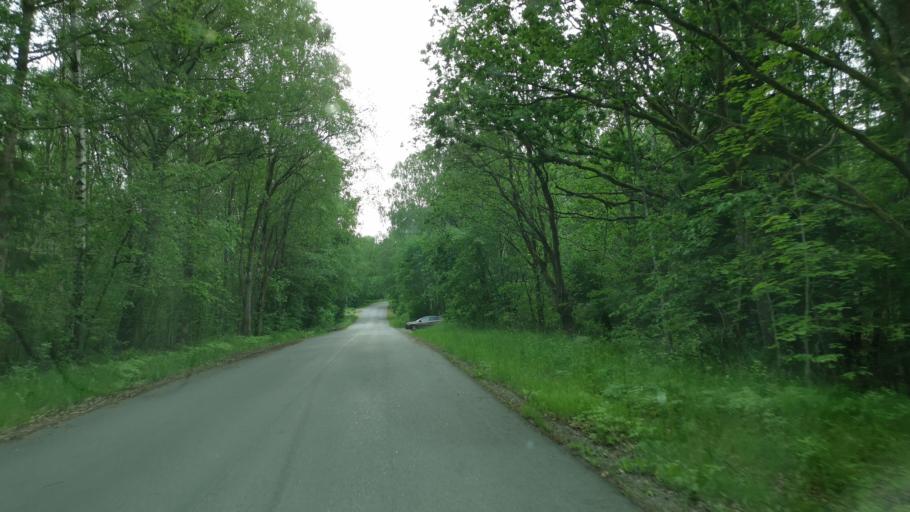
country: SE
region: Vaestra Goetaland
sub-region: Vanersborgs Kommun
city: Vargon
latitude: 58.3587
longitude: 12.3667
